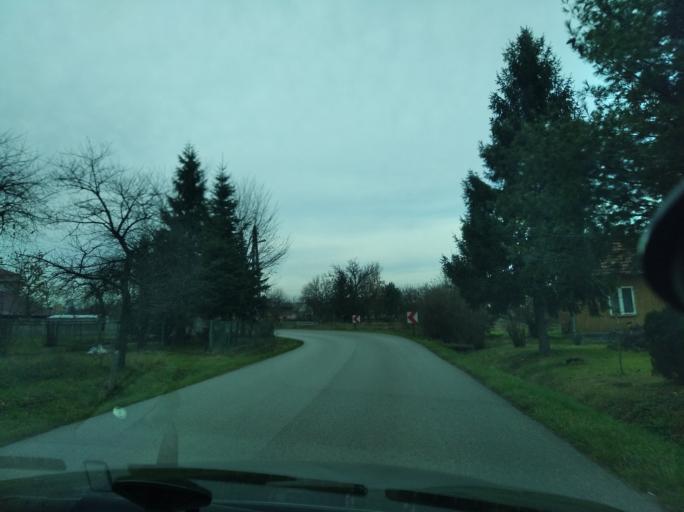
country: PL
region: Subcarpathian Voivodeship
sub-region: Powiat przeworski
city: Grzeska
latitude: 50.0917
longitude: 22.4451
